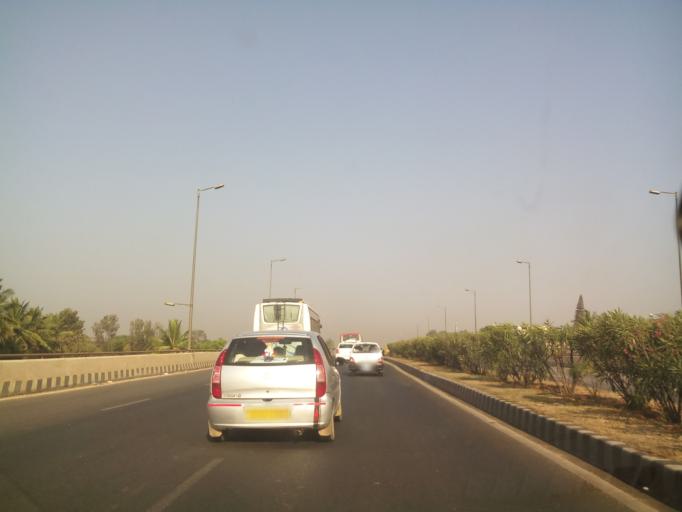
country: IN
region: Karnataka
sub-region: Bangalore Rural
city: Nelamangala
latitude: 13.0526
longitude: 77.4865
